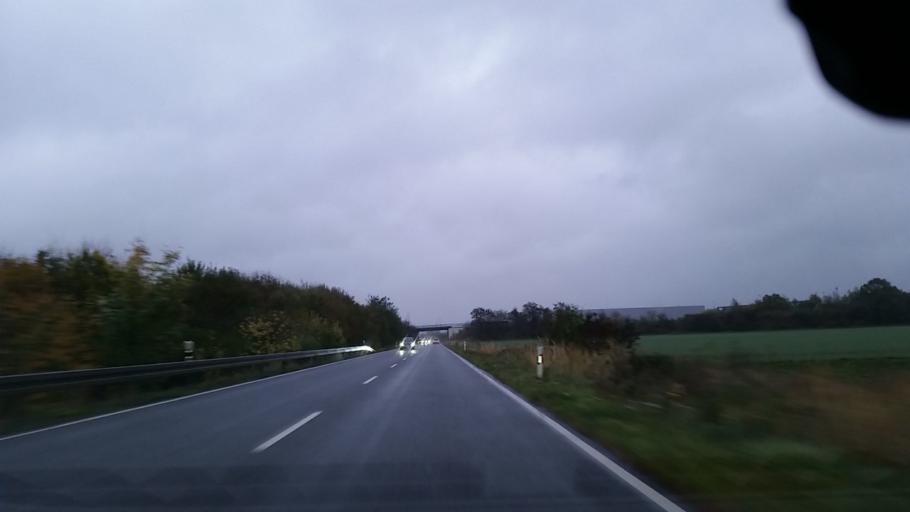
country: DE
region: Lower Saxony
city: Osloss
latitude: 52.4246
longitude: 10.6828
